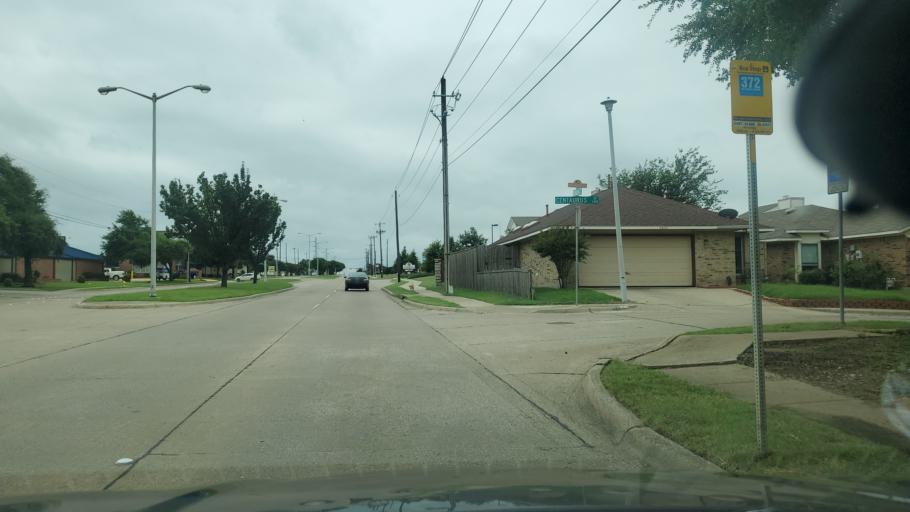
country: US
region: Texas
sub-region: Dallas County
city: Garland
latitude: 32.9486
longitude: -96.6654
